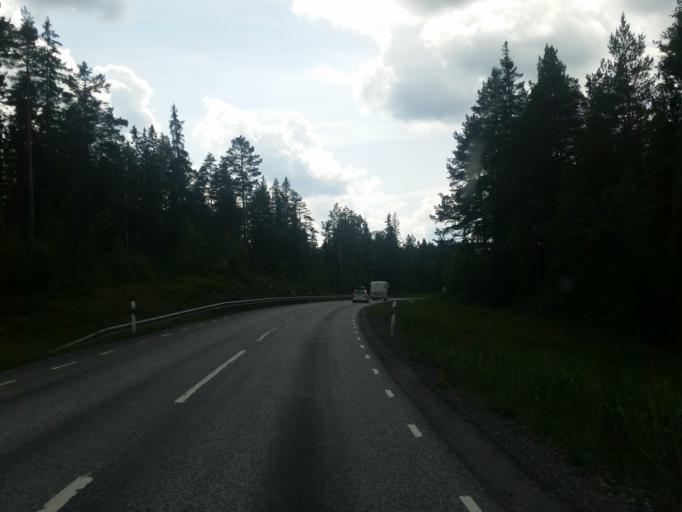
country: SE
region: OErebro
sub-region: Ljusnarsbergs Kommun
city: Kopparberg
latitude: 59.9386
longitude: 15.0263
